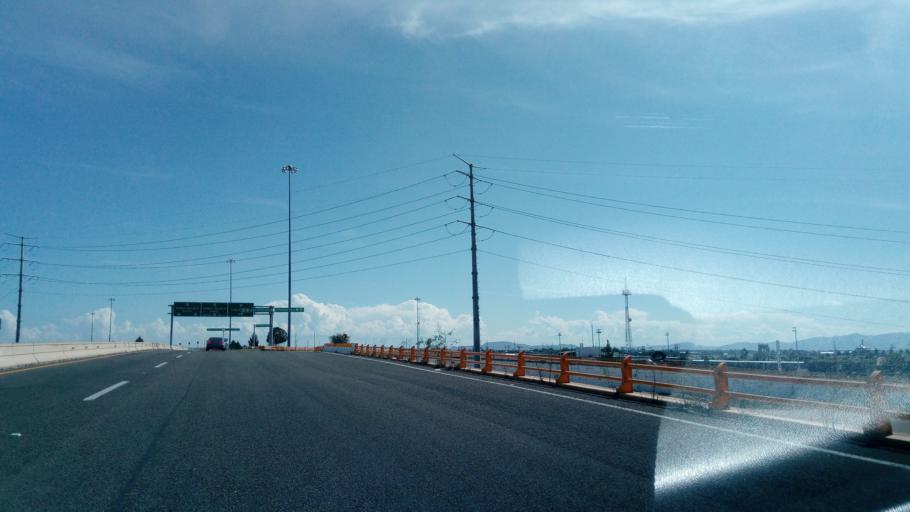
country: MX
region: Durango
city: Victoria de Durango
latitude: 24.0945
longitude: -104.5779
